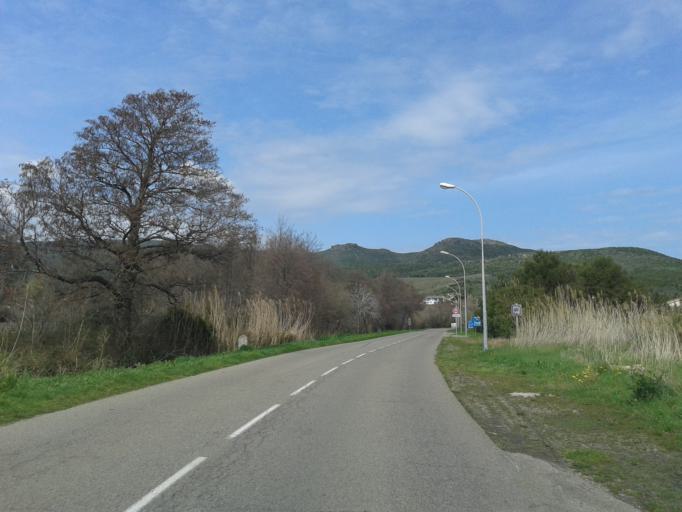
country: FR
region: Corsica
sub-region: Departement de la Haute-Corse
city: Brando
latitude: 42.8367
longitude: 9.4790
